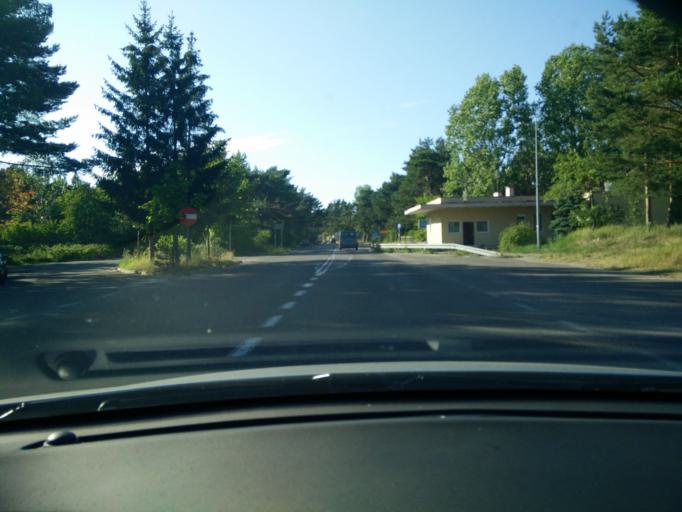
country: PL
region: Pomeranian Voivodeship
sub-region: Powiat pucki
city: Hel
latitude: 54.6187
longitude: 18.8020
